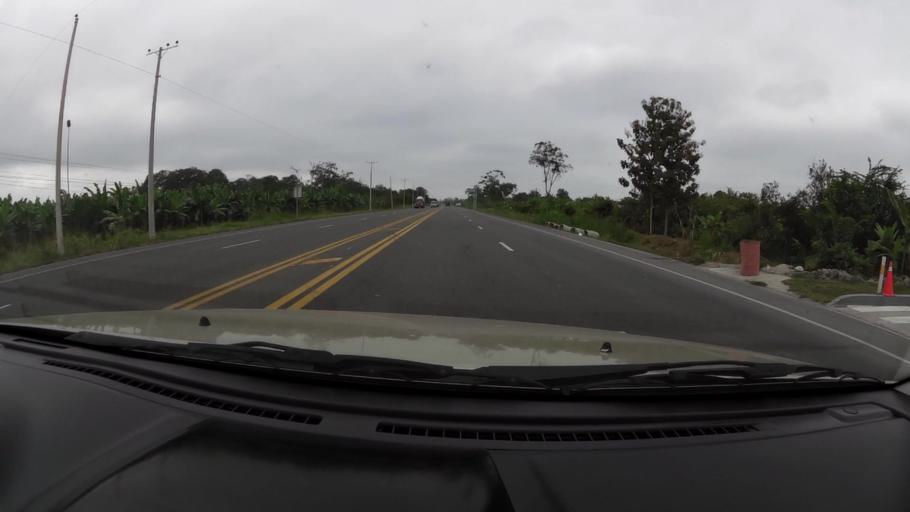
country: EC
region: Guayas
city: Naranjal
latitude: -2.5633
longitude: -79.5635
